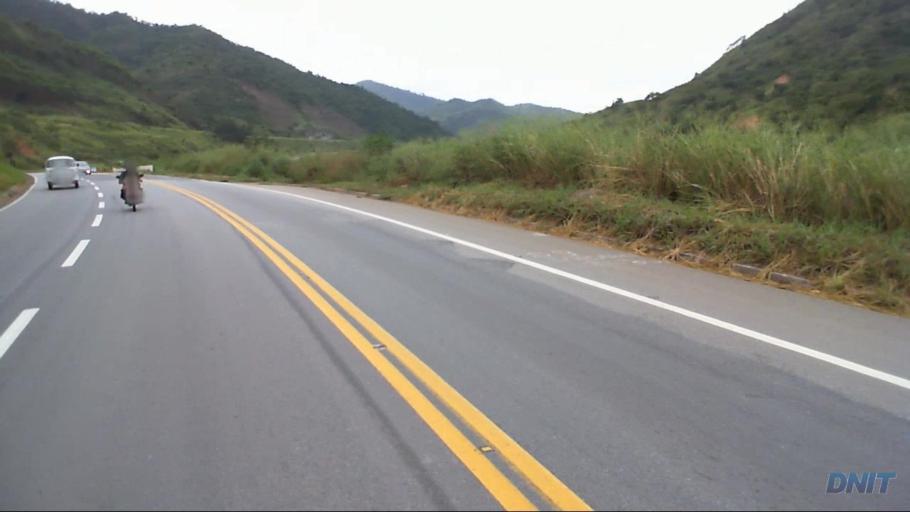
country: BR
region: Minas Gerais
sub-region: Timoteo
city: Timoteo
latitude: -19.6290
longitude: -42.8066
